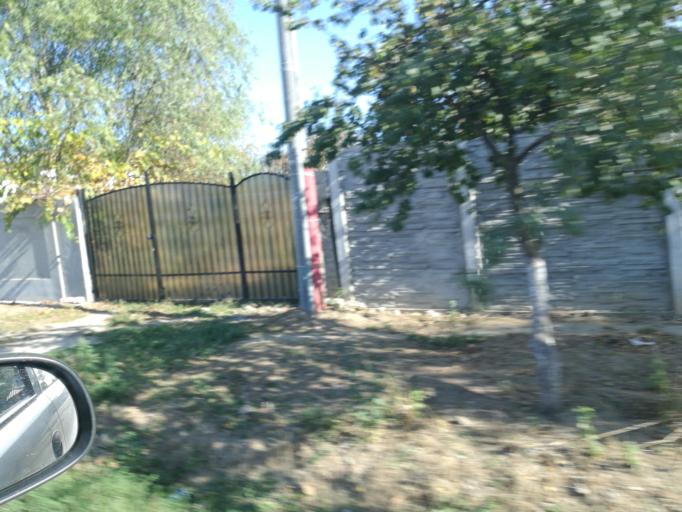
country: RO
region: Giurgiu
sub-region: Comuna Joita
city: Bacu
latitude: 44.4744
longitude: 25.8891
